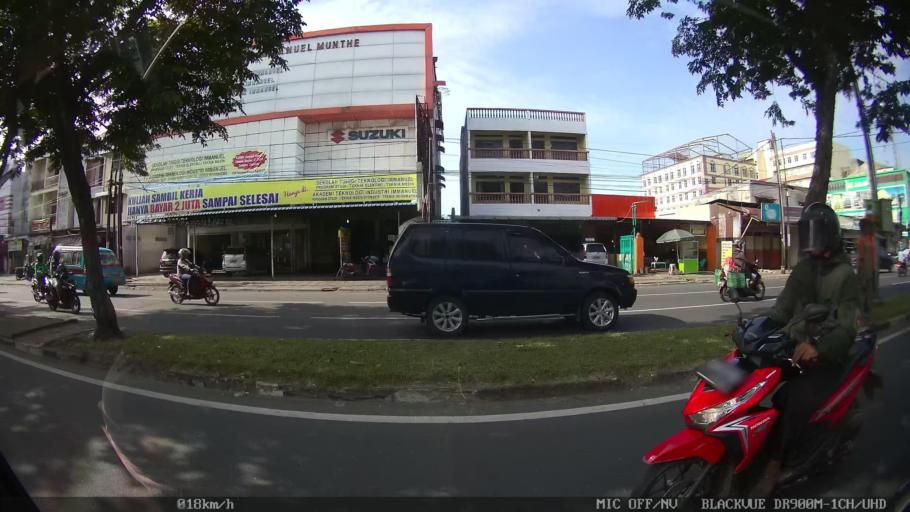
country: ID
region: North Sumatra
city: Medan
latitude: 3.5903
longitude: 98.6532
